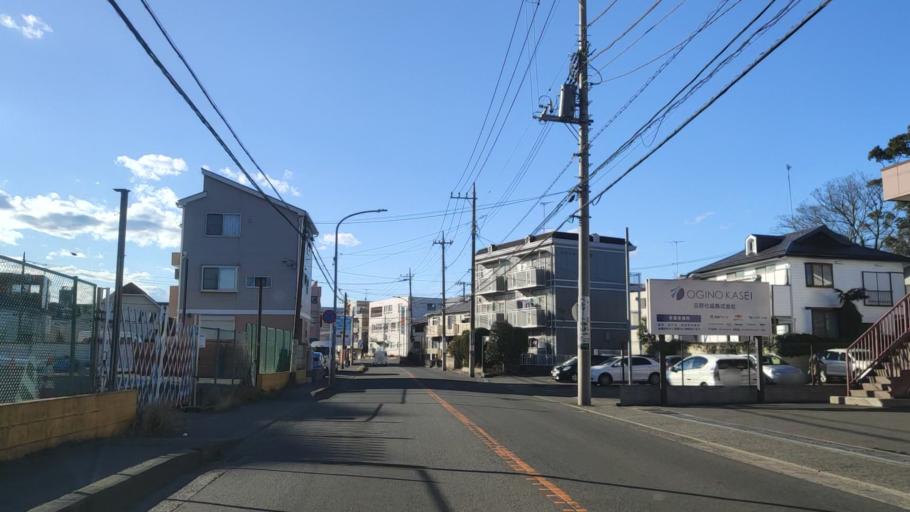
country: JP
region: Tokyo
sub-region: Machida-shi
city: Machida
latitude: 35.5185
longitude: 139.5474
